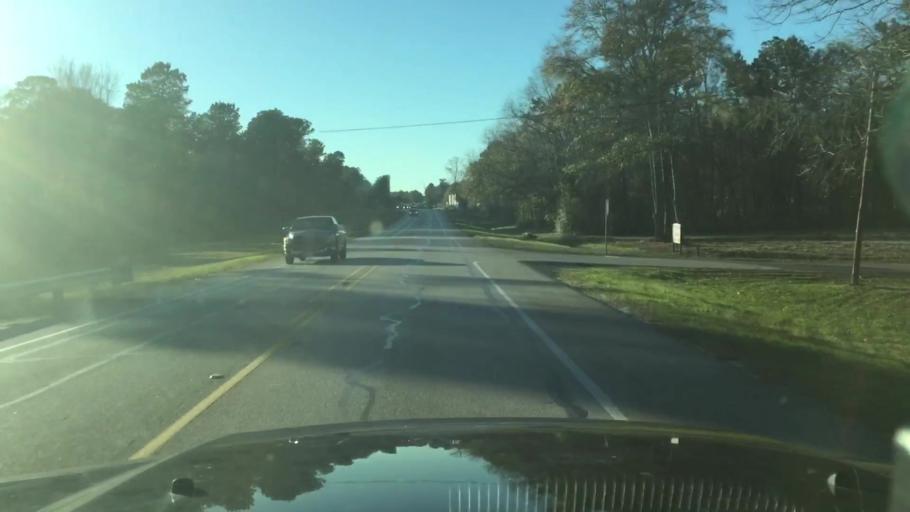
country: US
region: Texas
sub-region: Montgomery County
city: Conroe
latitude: 30.3156
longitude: -95.5233
